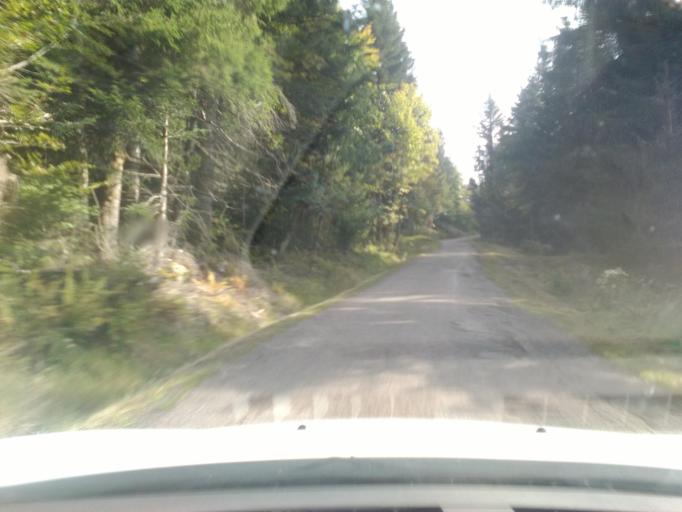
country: FR
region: Lorraine
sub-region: Departement des Vosges
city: Gerardmer
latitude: 48.0498
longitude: 6.8892
